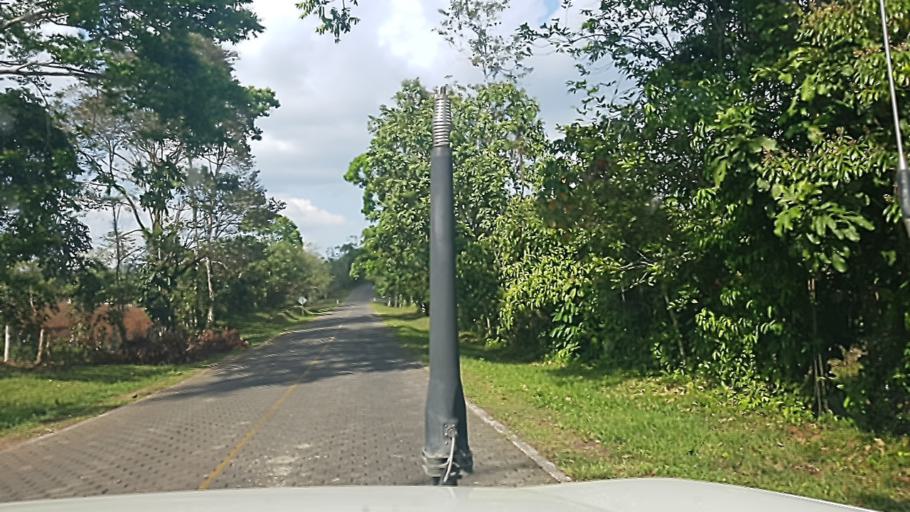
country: NI
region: Atlantico Sur
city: Nueva Guinea
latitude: 11.7074
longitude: -84.3661
